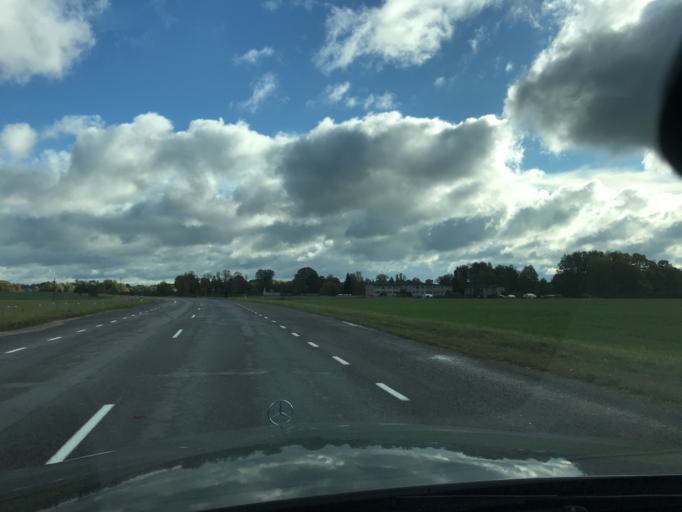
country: EE
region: Valgamaa
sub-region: Torva linn
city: Torva
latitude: 57.9778
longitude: 25.9802
